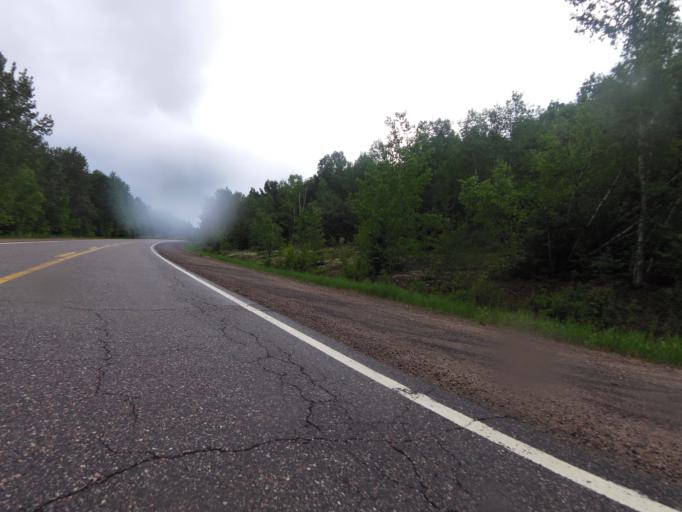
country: CA
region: Quebec
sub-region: Outaouais
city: Shawville
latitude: 45.9068
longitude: -76.2675
